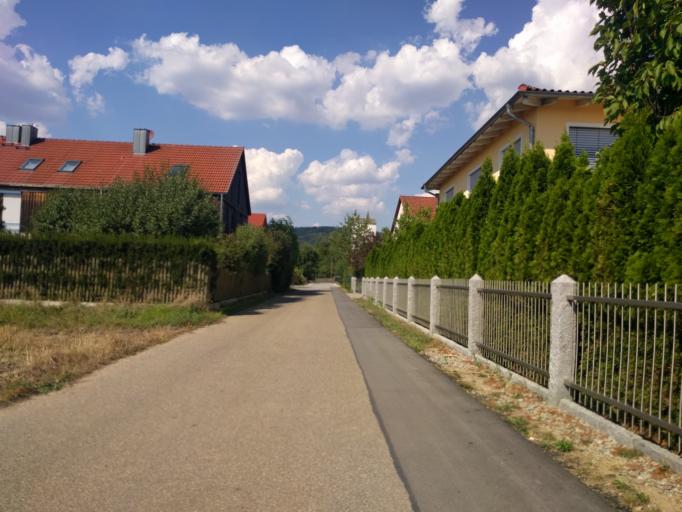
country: DE
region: Bavaria
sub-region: Upper Palatinate
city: Mintraching
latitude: 49.0066
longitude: 12.2714
